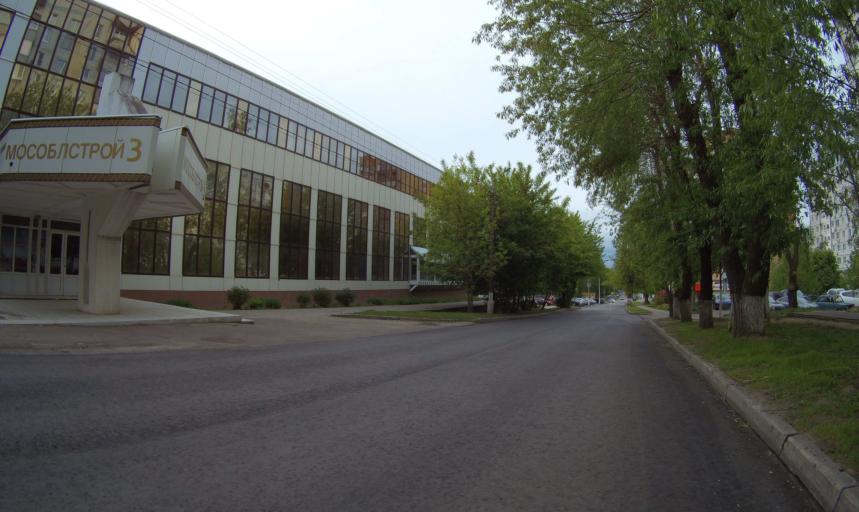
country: RU
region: Moskovskaya
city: Kolomna
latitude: 55.0839
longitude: 38.7727
